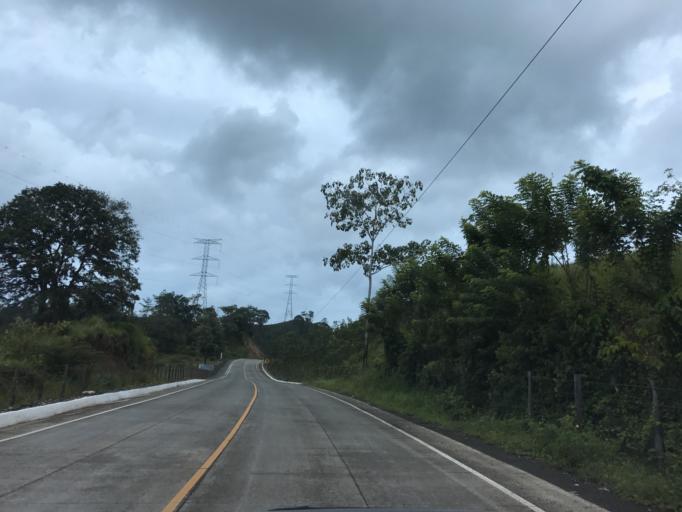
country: GT
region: Izabal
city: Morales
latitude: 15.6354
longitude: -89.0450
